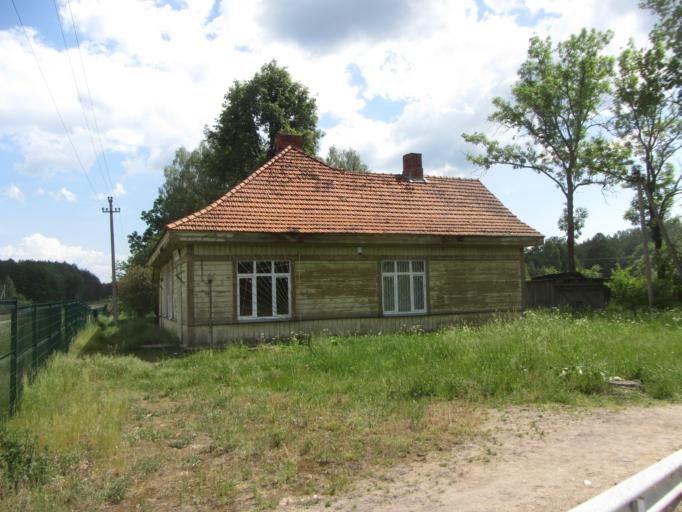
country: LT
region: Kauno apskritis
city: Jonava
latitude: 55.0332
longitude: 24.2679
